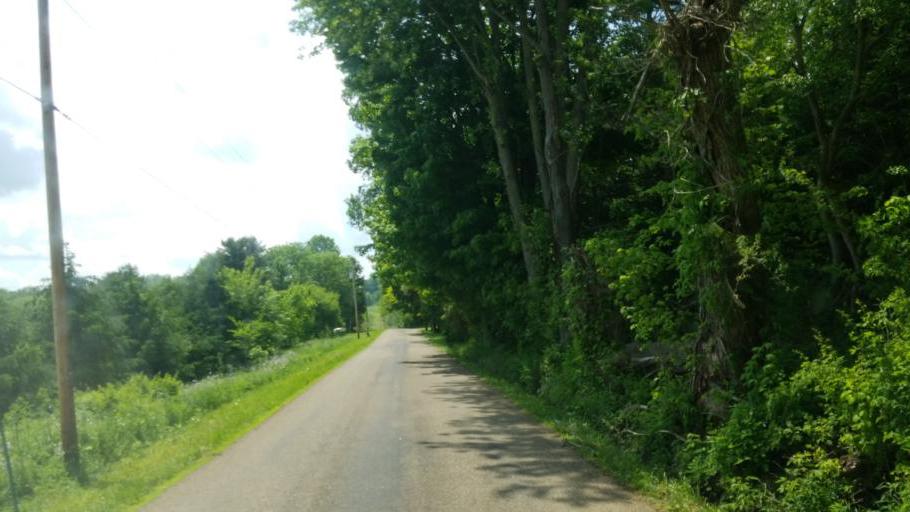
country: US
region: Ohio
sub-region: Ashland County
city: Loudonville
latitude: 40.6606
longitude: -82.3611
